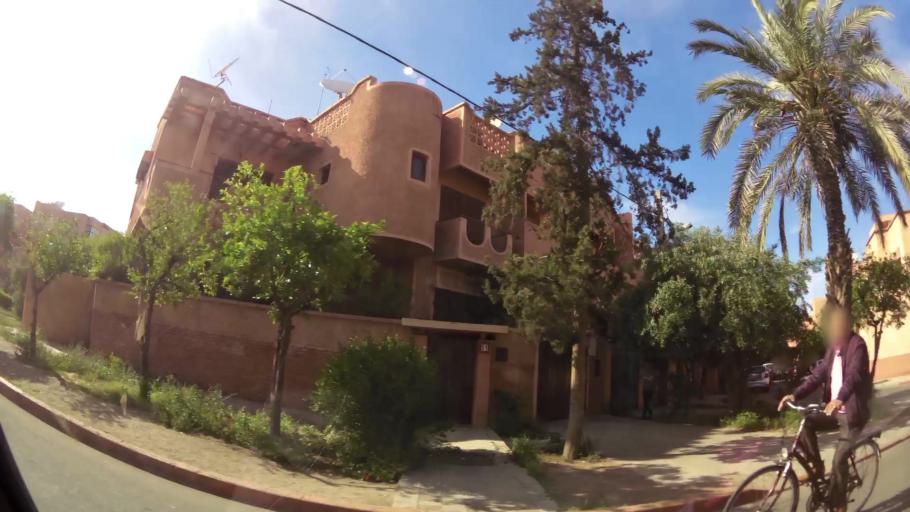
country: MA
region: Marrakech-Tensift-Al Haouz
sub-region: Marrakech
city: Marrakesh
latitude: 31.6535
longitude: -8.0083
